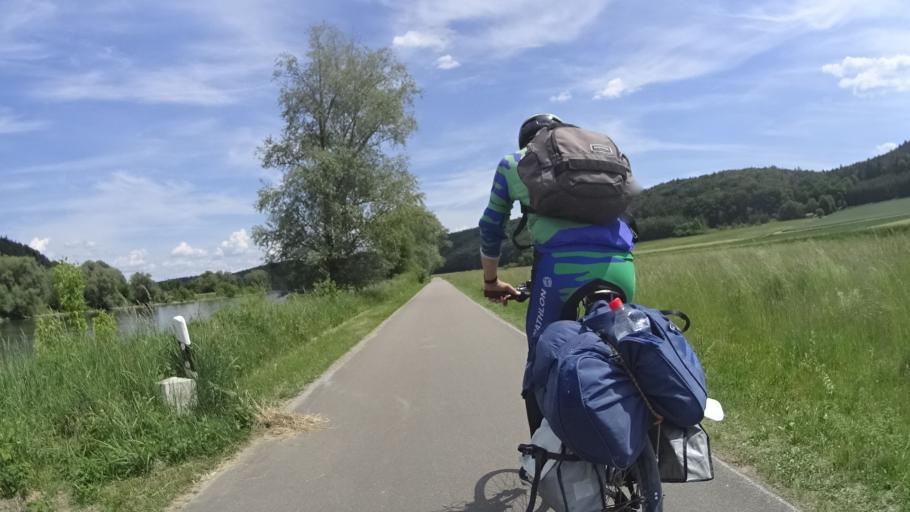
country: DE
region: Bavaria
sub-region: Upper Palatinate
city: Sinzing
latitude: 48.9678
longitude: 12.0168
